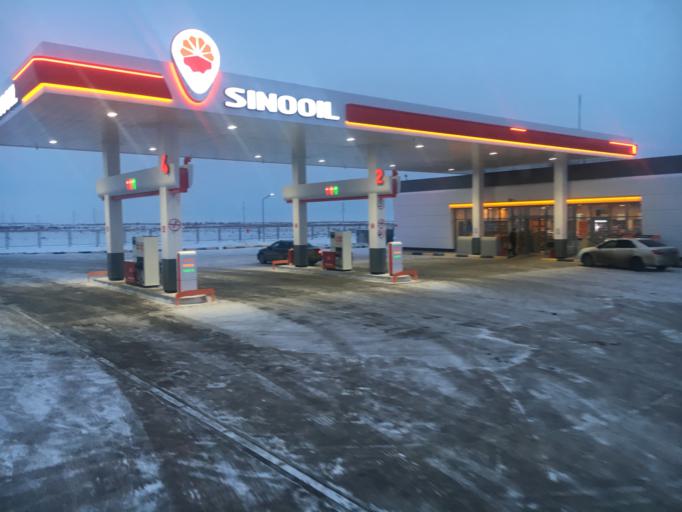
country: KZ
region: Qyzylorda
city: Ayteke Bi
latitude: 45.8722
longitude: 62.1588
